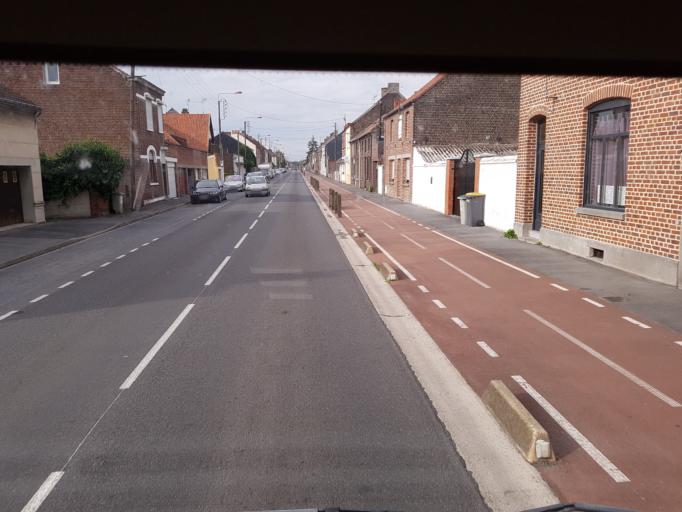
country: FR
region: Nord-Pas-de-Calais
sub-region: Departement du Nord
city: Vieux-Conde
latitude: 50.4671
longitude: 3.5710
